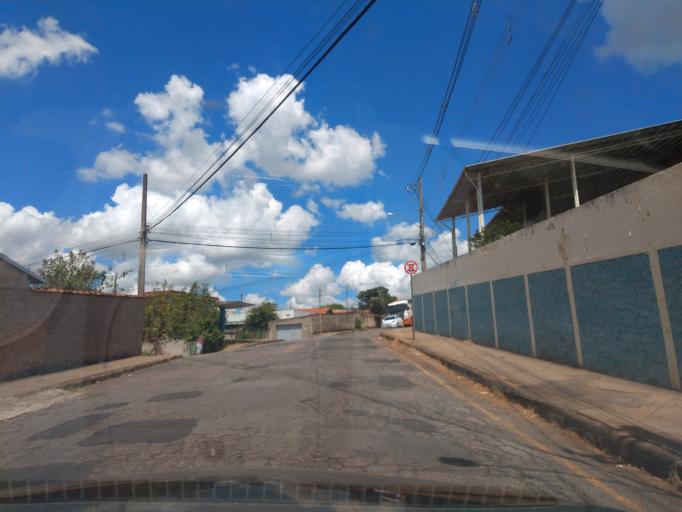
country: BR
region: Minas Gerais
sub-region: Tres Coracoes
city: Tres Coracoes
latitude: -21.6869
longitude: -45.2521
